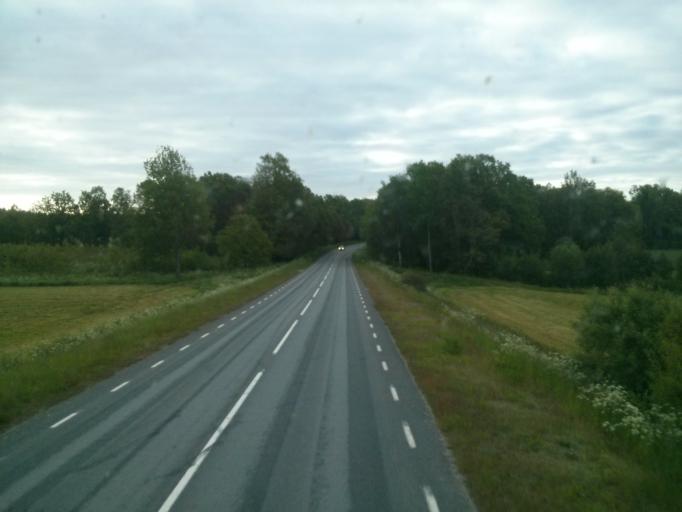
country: SE
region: Blekinge
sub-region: Ronneby Kommun
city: Kallinge
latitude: 56.2841
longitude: 15.2263
